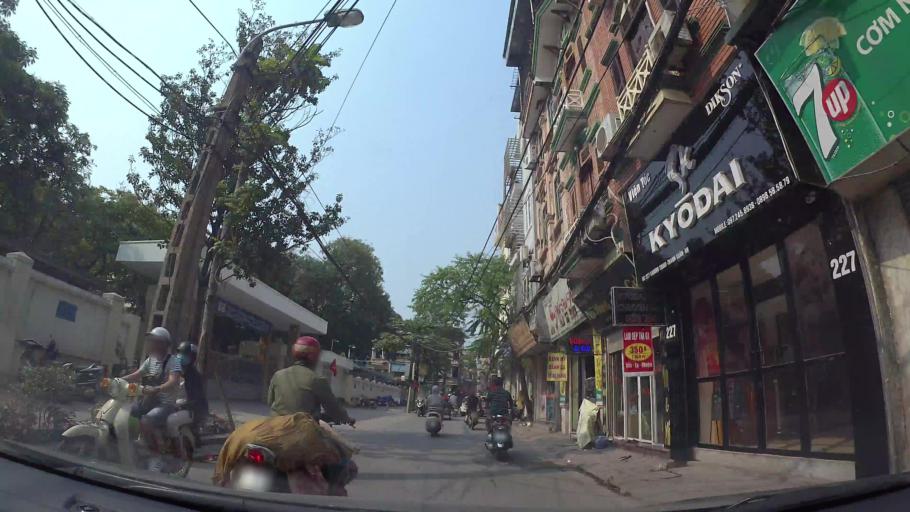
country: VN
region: Ha Noi
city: Thanh Xuan
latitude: 20.9966
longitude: 105.8180
